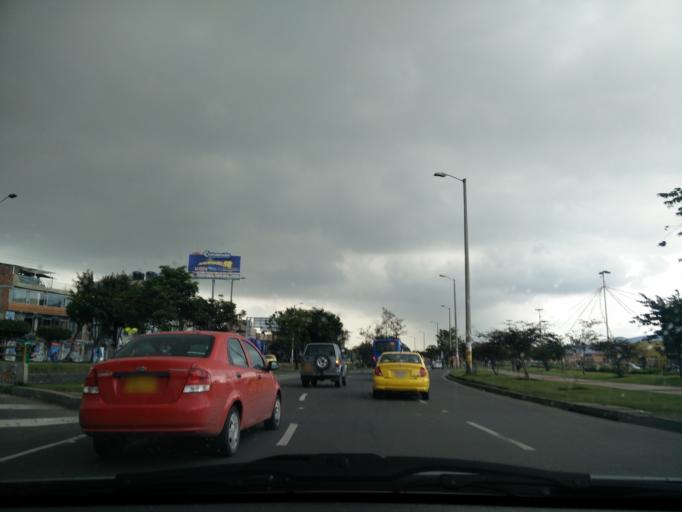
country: CO
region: Cundinamarca
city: Cota
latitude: 4.7473
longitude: -74.0969
